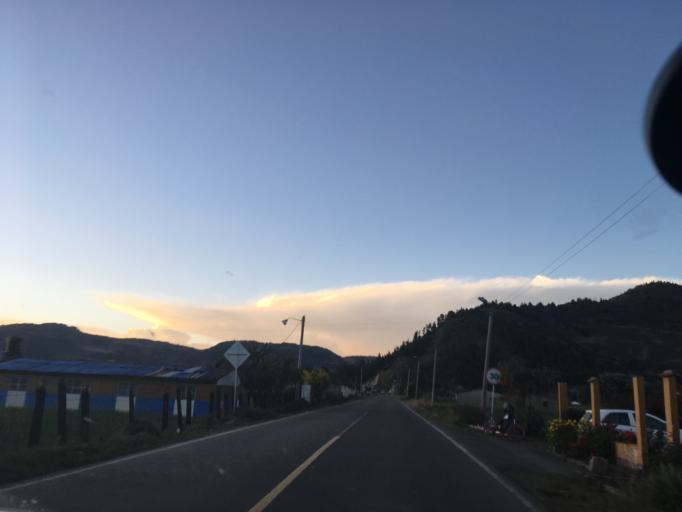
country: CO
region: Boyaca
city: Aquitania
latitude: 5.5827
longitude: -72.8958
